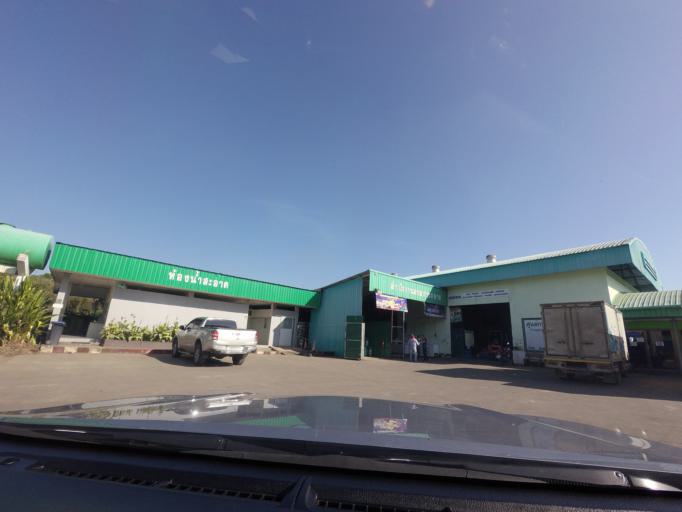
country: TH
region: Phrae
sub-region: Amphoe Wang Chin
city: Wang Chin
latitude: 17.9056
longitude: 99.6029
